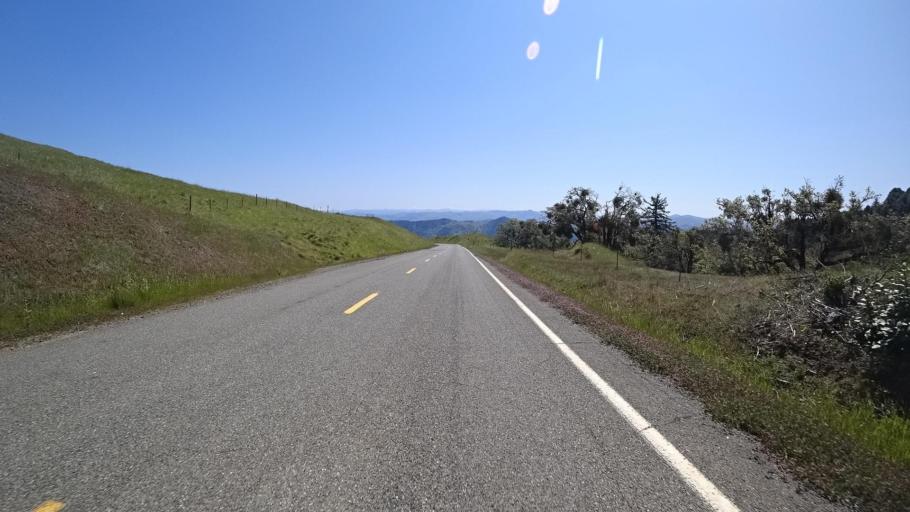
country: US
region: California
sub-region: Humboldt County
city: Redway
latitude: 40.1040
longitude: -123.6806
